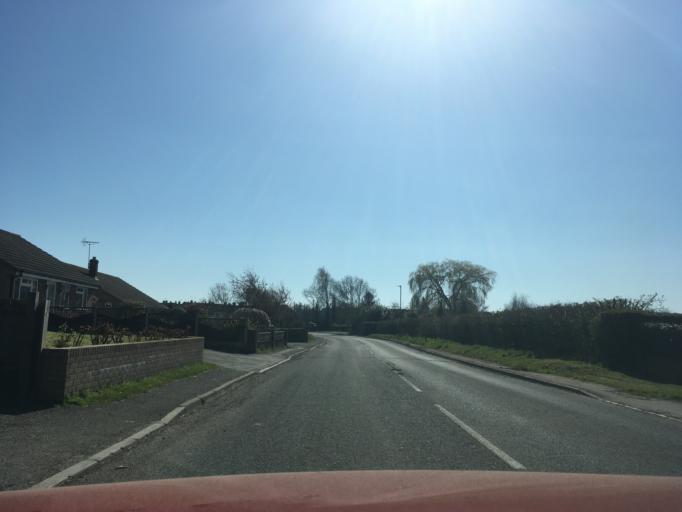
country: GB
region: England
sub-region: Gloucestershire
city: Berkeley
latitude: 51.6934
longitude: -2.4687
